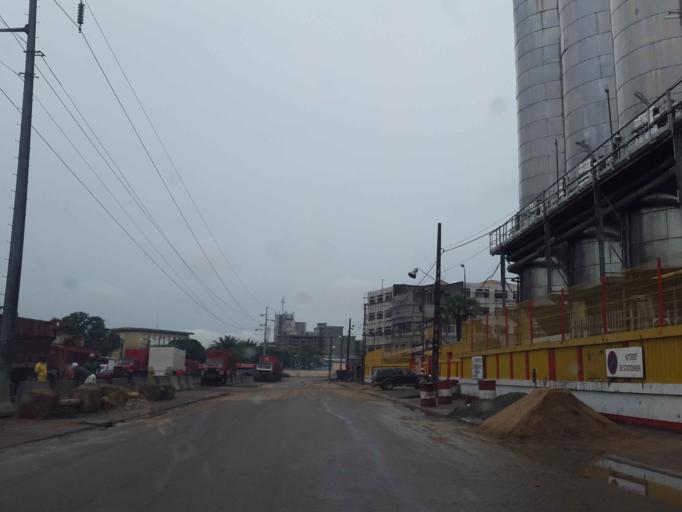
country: CM
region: Littoral
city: Douala
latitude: 4.0331
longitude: 9.6936
